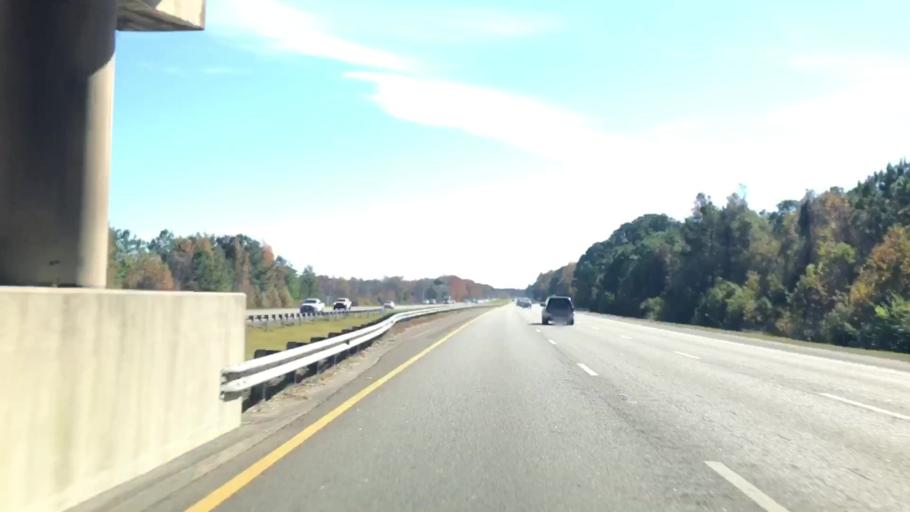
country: US
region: South Carolina
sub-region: Berkeley County
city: Ladson
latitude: 32.9984
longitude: -80.0940
